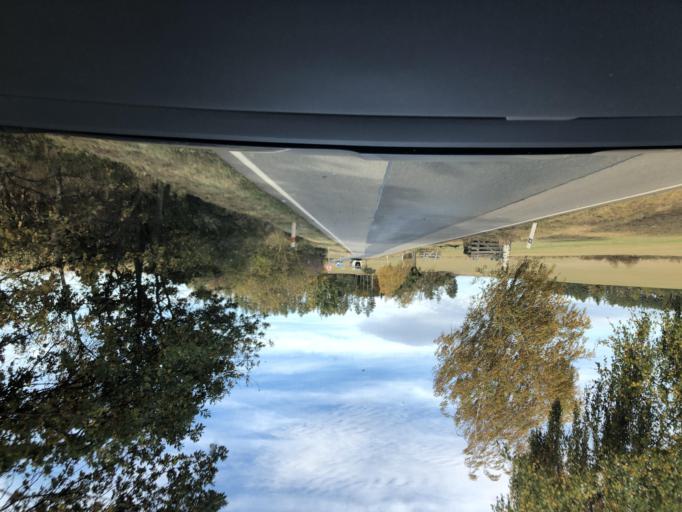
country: CZ
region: Central Bohemia
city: Divisov
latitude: 49.7837
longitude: 14.8199
